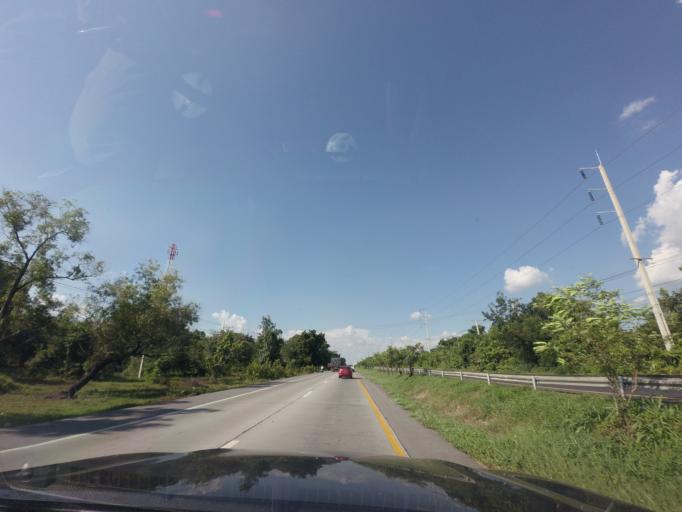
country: TH
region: Nakhon Ratchasima
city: Sida
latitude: 15.5600
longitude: 102.5511
